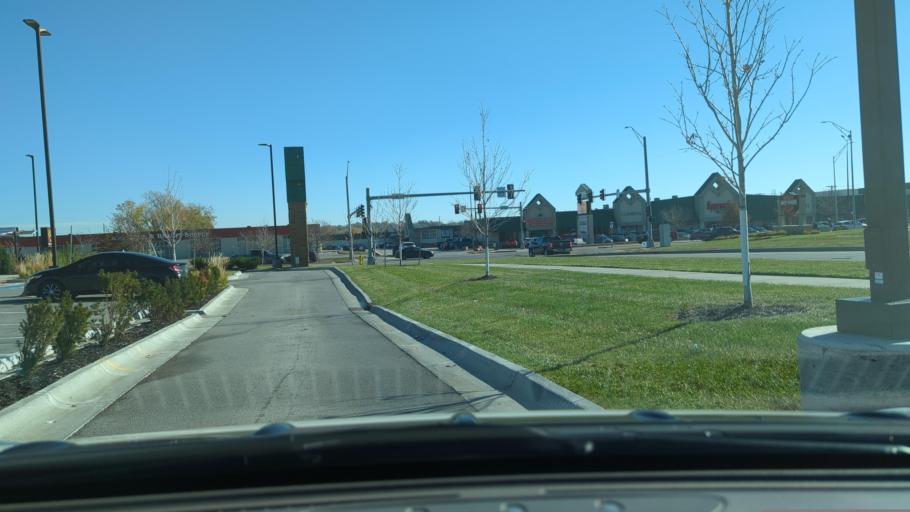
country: US
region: Nebraska
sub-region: Douglas County
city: Ralston
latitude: 41.2108
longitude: -96.0249
